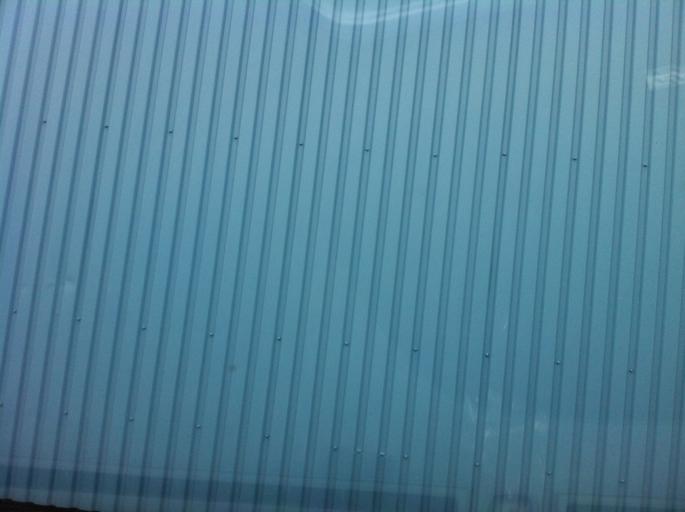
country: SE
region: Kalmar
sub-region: Vasterviks Kommun
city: Overum
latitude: 57.9126
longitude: 16.2778
